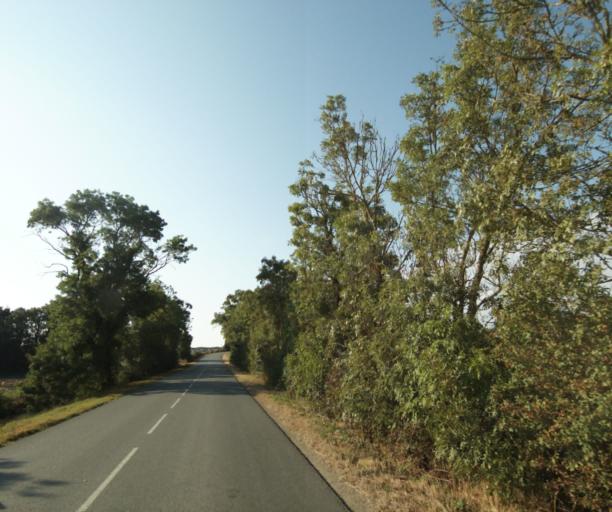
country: FR
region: Poitou-Charentes
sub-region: Departement de la Charente-Maritime
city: Muron
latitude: 45.9878
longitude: -0.8390
